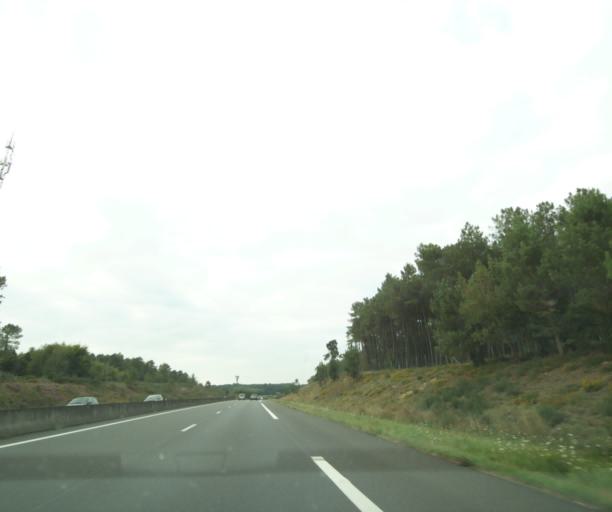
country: FR
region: Pays de la Loire
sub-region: Departement de la Sarthe
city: Luceau
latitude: 47.7057
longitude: 0.3502
